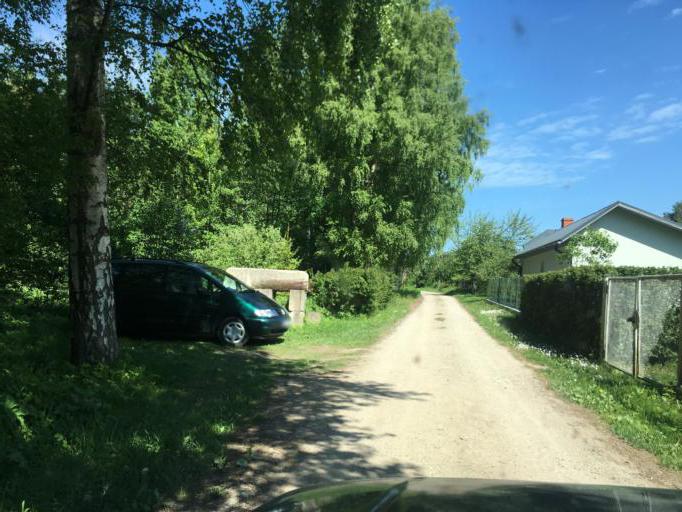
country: LV
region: Ventspils
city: Ventspils
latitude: 57.4545
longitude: 21.6531
